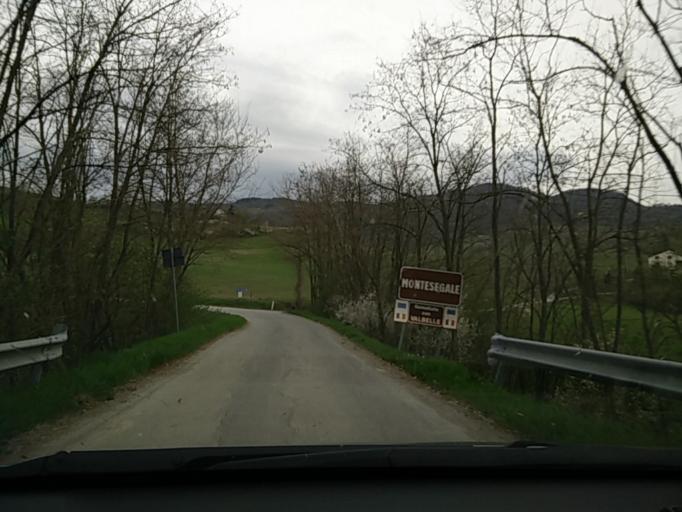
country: IT
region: Lombardy
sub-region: Provincia di Pavia
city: Susella
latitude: 44.9005
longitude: 9.1044
